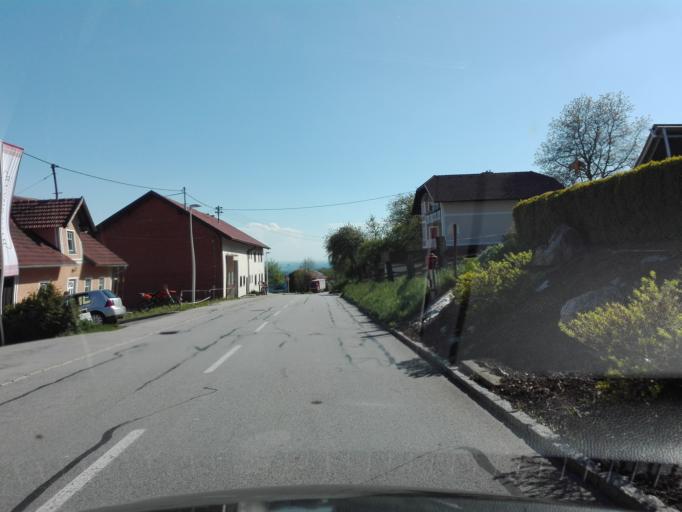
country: DE
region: Bavaria
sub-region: Lower Bavaria
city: Obernzell
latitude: 48.4428
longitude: 13.6546
